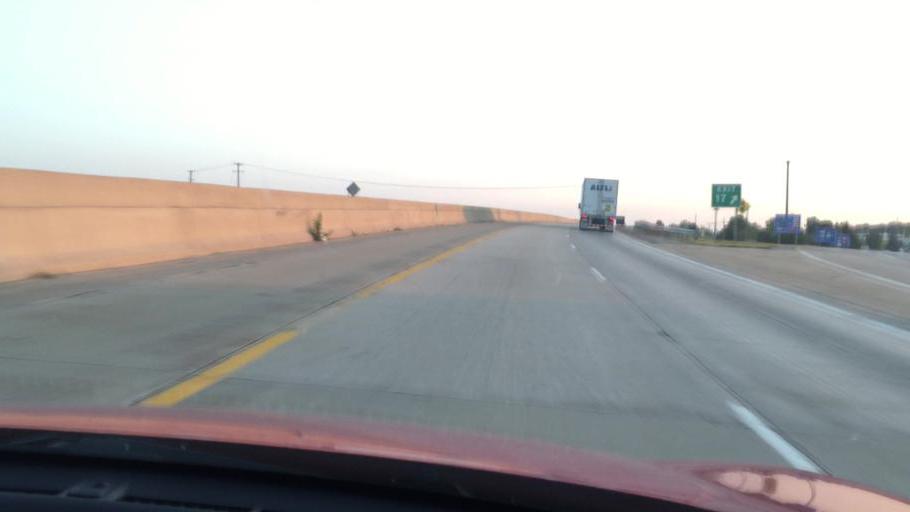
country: US
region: Michigan
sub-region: Monroe County
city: Dundee
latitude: 41.9571
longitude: -83.6722
